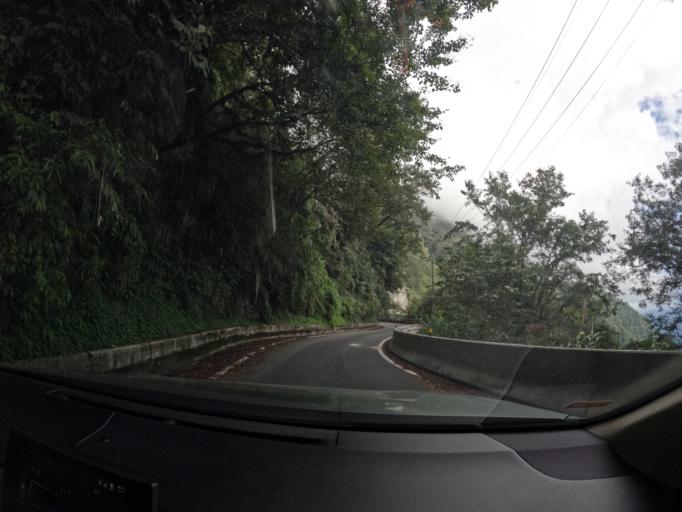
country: TW
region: Taiwan
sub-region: Taitung
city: Taitung
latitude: 23.2406
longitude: 121.0010
